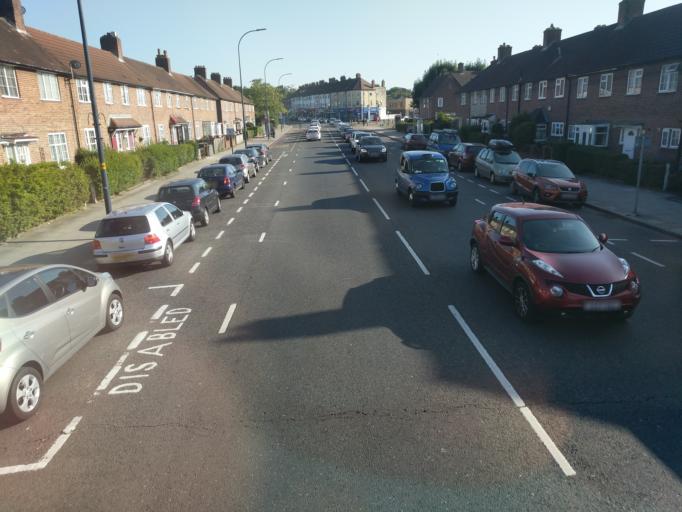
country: GB
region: England
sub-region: Greater London
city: Bromley
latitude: 51.4228
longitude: -0.0028
